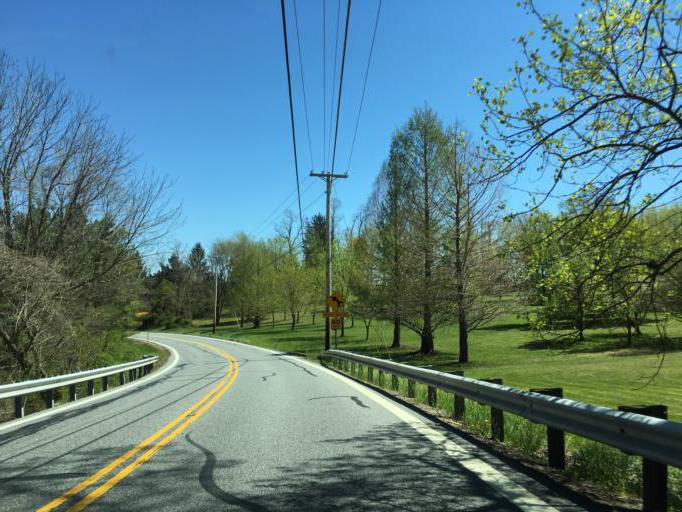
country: US
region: Maryland
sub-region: Baltimore County
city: Hunt Valley
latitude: 39.5823
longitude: -76.6297
